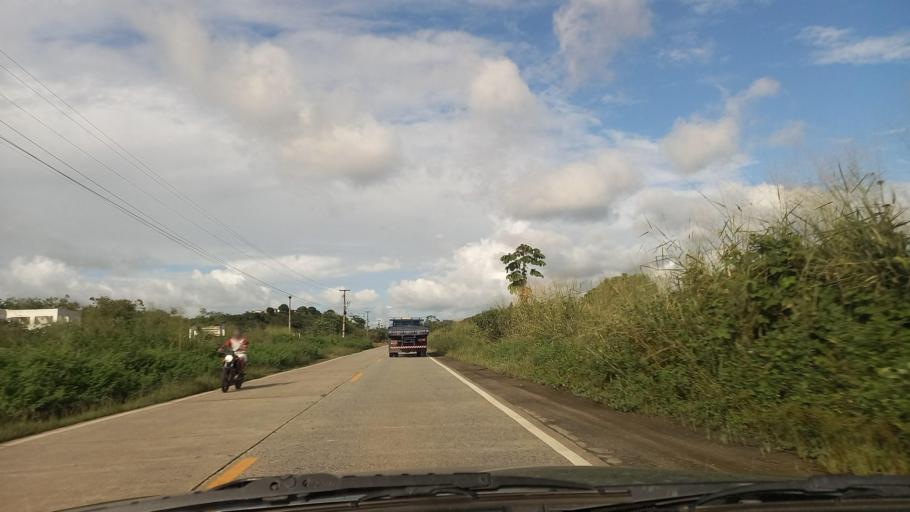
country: BR
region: Pernambuco
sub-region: Palmares
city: Palmares
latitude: -8.6914
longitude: -35.6237
